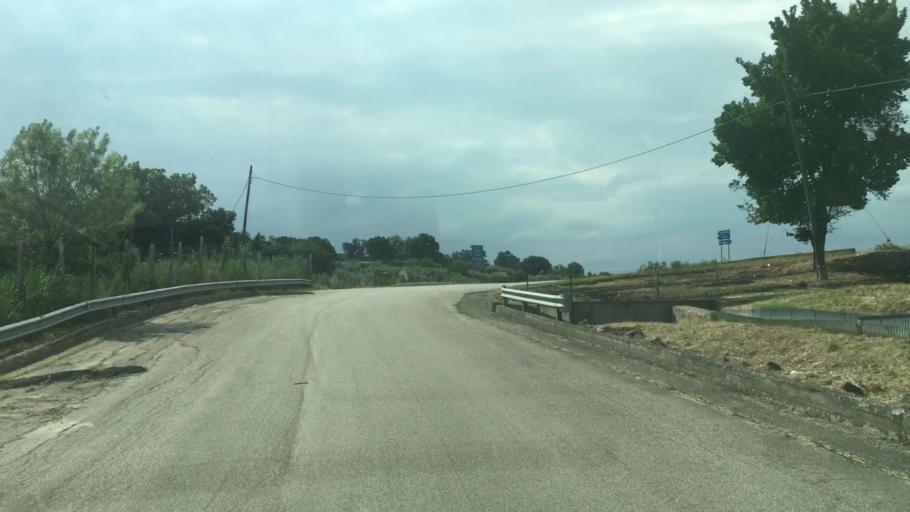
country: IT
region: Basilicate
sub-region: Provincia di Matera
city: San Mauro Forte
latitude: 40.4793
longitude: 16.2670
